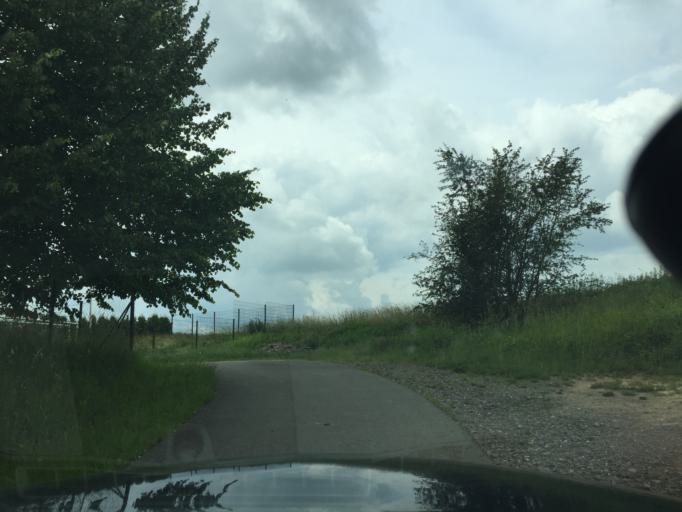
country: DE
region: Thuringia
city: Schmolln
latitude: 50.8867
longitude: 12.3342
